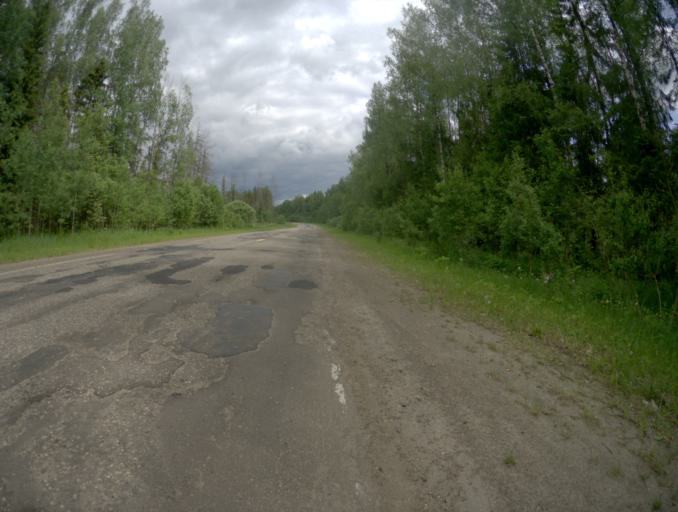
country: RU
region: Ivanovo
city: Arkhipovka
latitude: 56.6155
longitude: 41.2626
